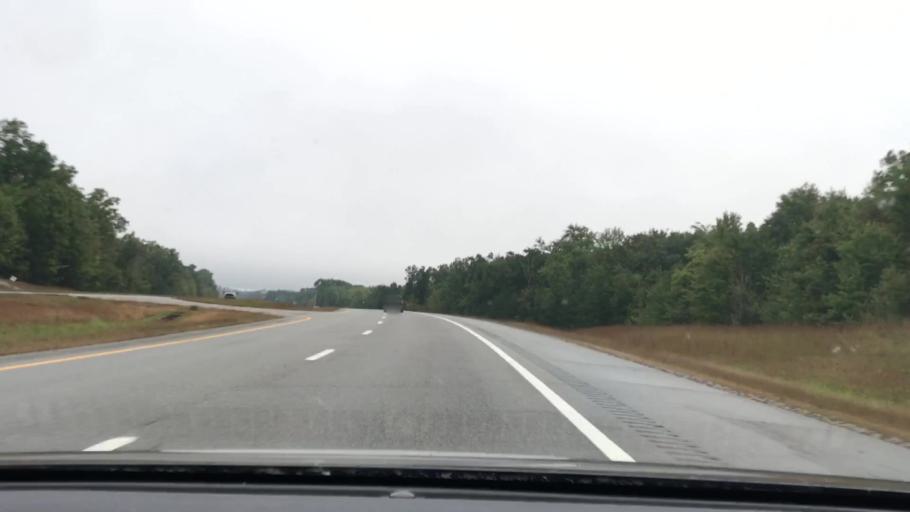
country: US
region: Tennessee
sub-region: Fentress County
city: Grimsley
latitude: 36.3324
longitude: -84.9581
